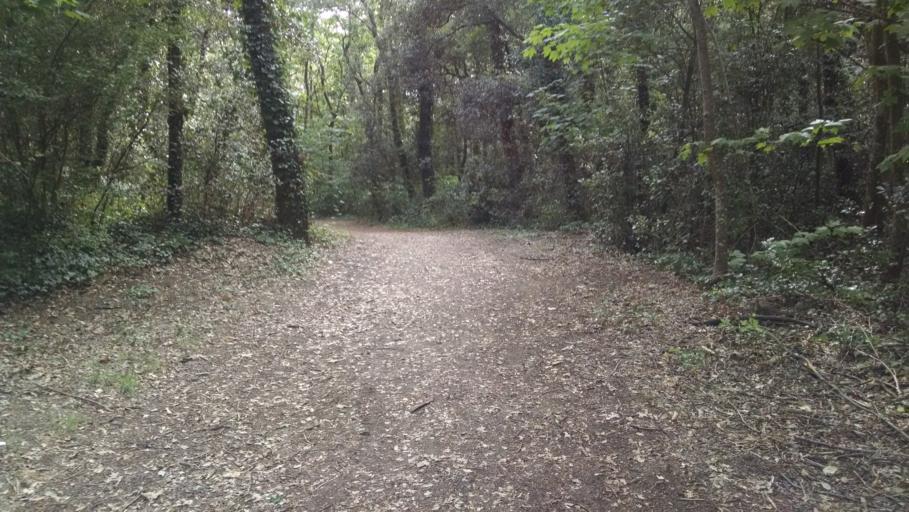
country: FR
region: Pays de la Loire
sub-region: Departement de la Vendee
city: Jard-sur-Mer
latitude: 46.4146
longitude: -1.5548
